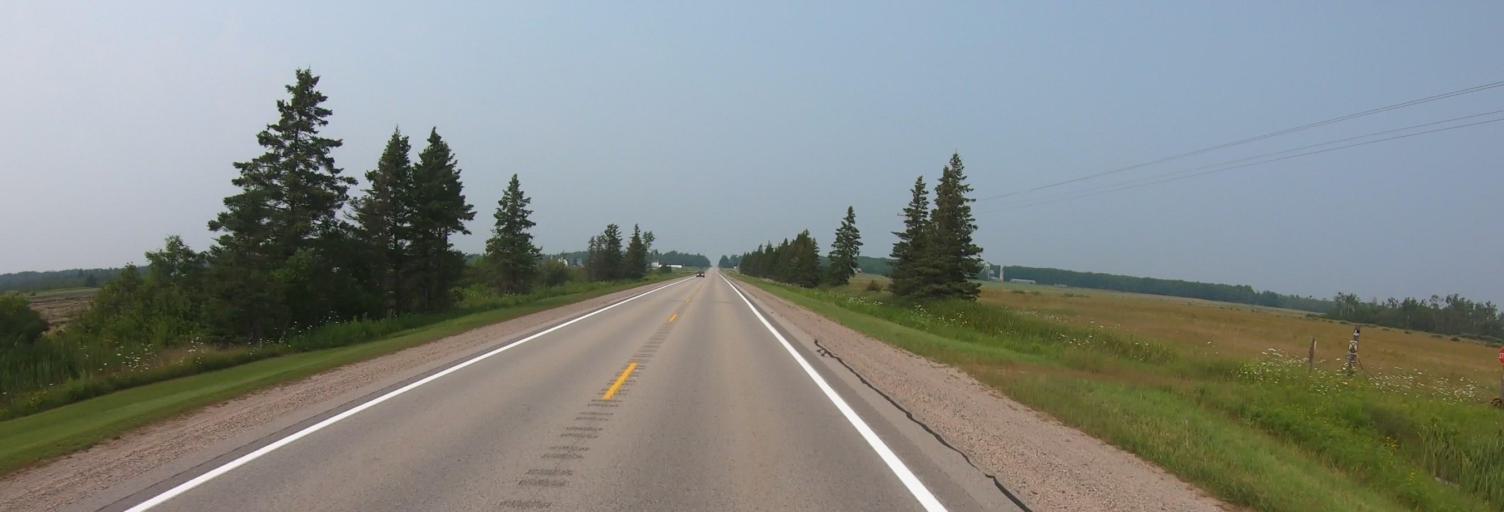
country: US
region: Michigan
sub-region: Chippewa County
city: Sault Ste. Marie
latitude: 46.1978
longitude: -84.3635
